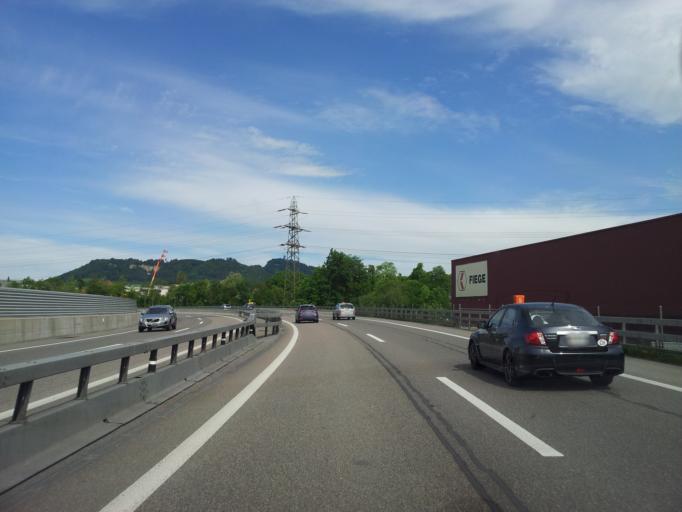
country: CH
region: Bern
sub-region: Bern-Mittelland District
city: Bolligen
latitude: 46.9701
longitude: 7.4678
